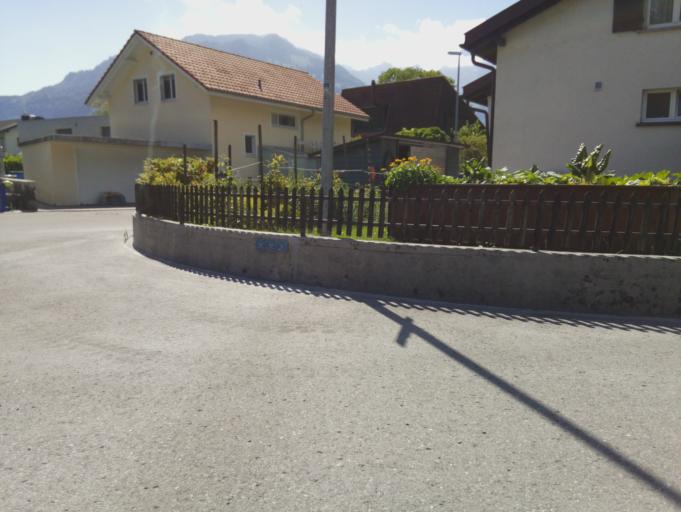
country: CH
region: Glarus
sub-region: Glarus
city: Niederurnen
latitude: 47.1247
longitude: 9.0550
